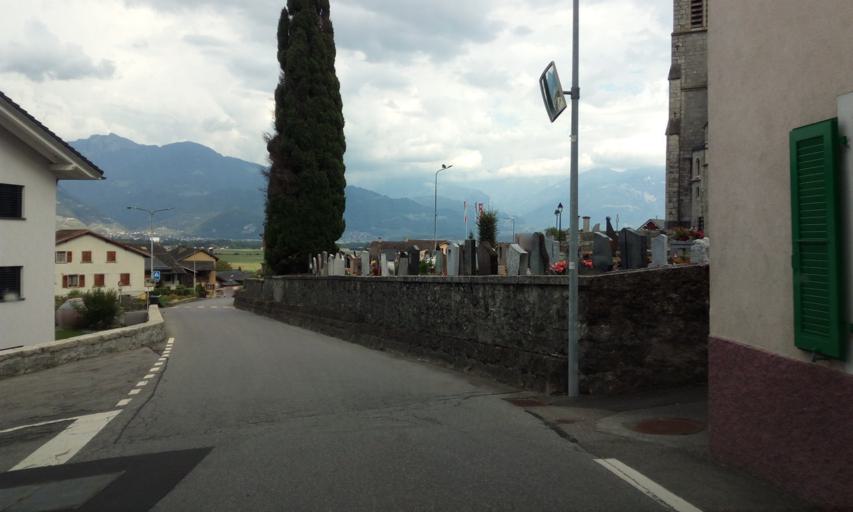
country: CH
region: Valais
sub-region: Monthey District
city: Vionnaz
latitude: 46.3094
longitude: 6.8990
